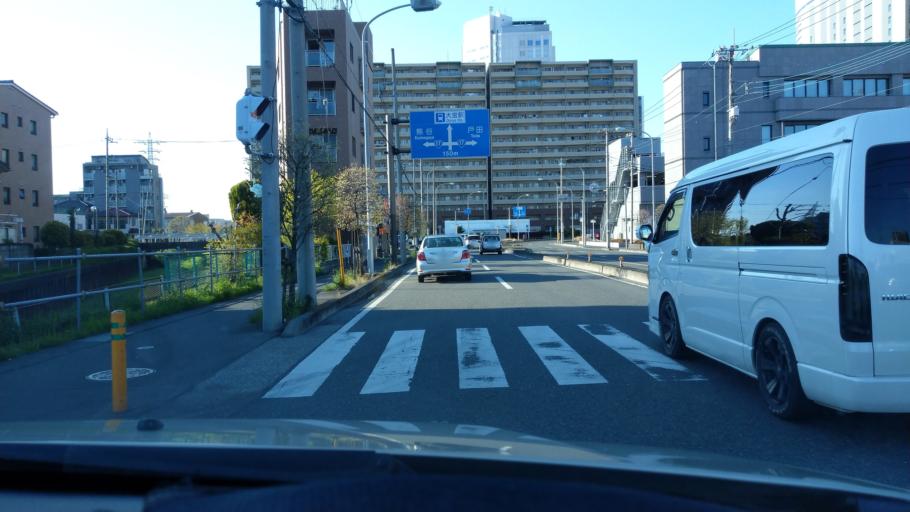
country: JP
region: Saitama
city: Yono
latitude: 35.9010
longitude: 139.6191
